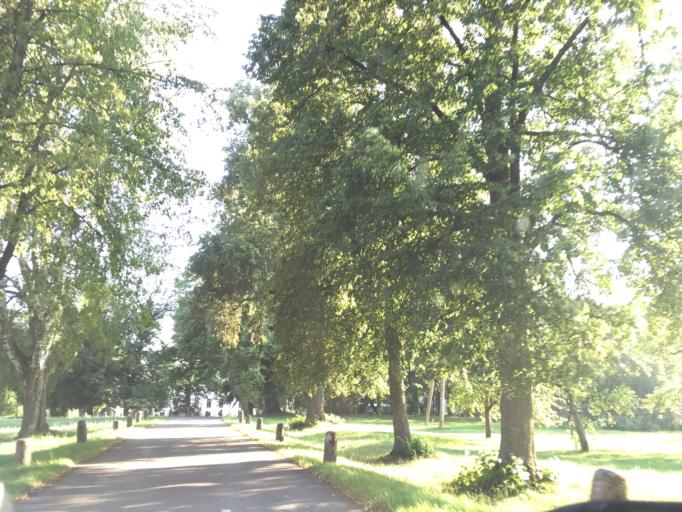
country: LV
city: Tervete
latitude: 56.4222
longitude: 23.5435
